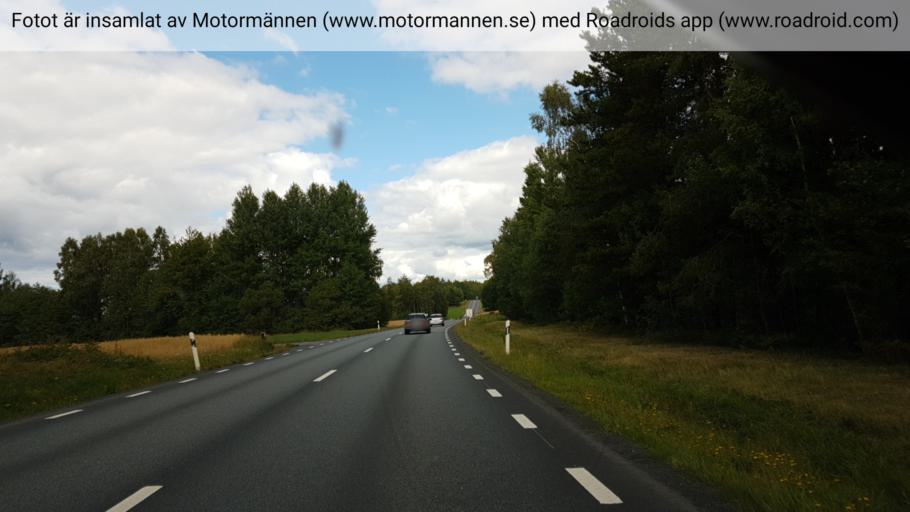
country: SE
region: Joenkoeping
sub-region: Aneby Kommun
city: Aneby
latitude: 57.8521
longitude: 14.8619
